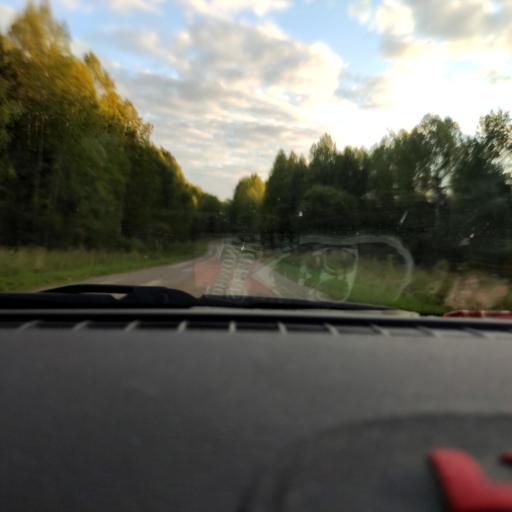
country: RU
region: Perm
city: Pavlovskiy
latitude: 57.9902
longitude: 54.8779
